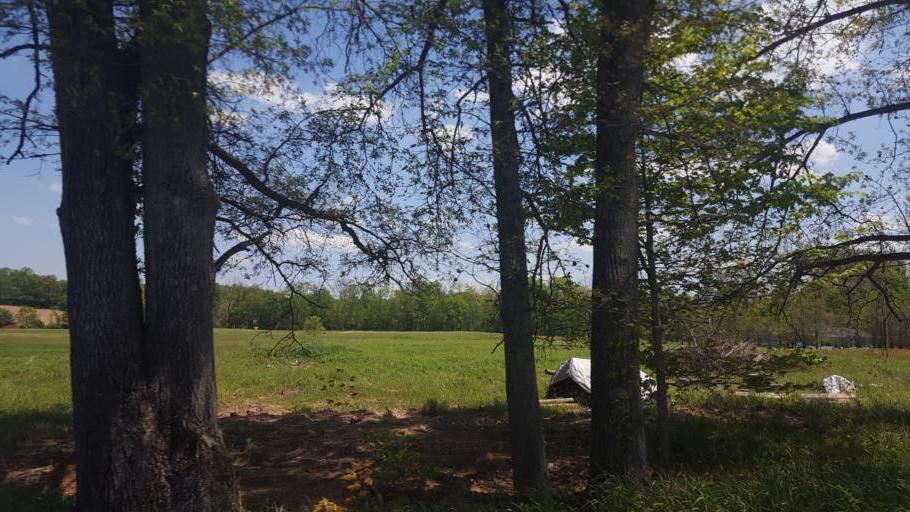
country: US
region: Ohio
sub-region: Knox County
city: Oak Hill
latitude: 40.2962
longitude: -82.2422
